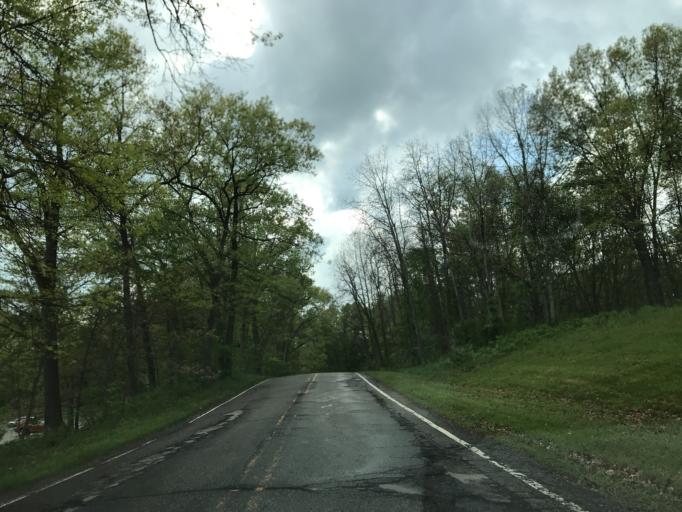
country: US
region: Michigan
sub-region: Oakland County
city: South Lyon
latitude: 42.5348
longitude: -83.6491
